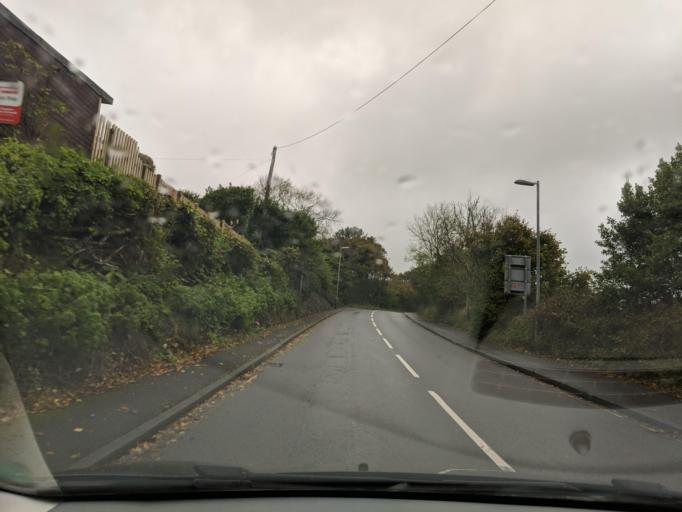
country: GB
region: England
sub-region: Cornwall
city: Bodmin
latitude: 50.4651
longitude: -4.7198
